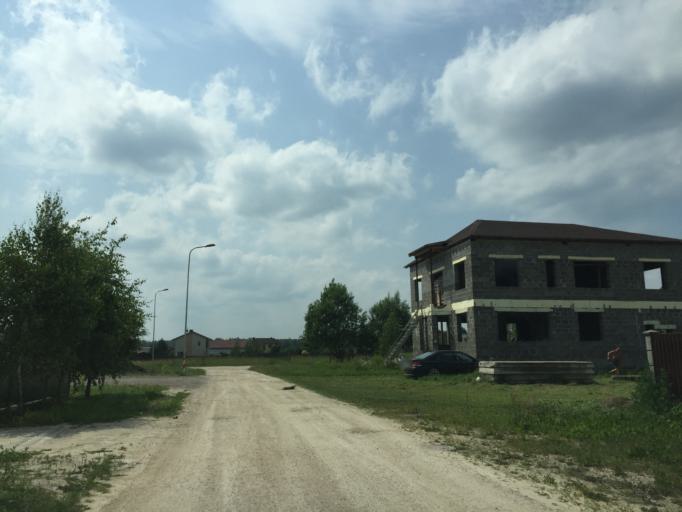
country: LV
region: Olaine
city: Olaine
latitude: 56.7774
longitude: 23.9235
